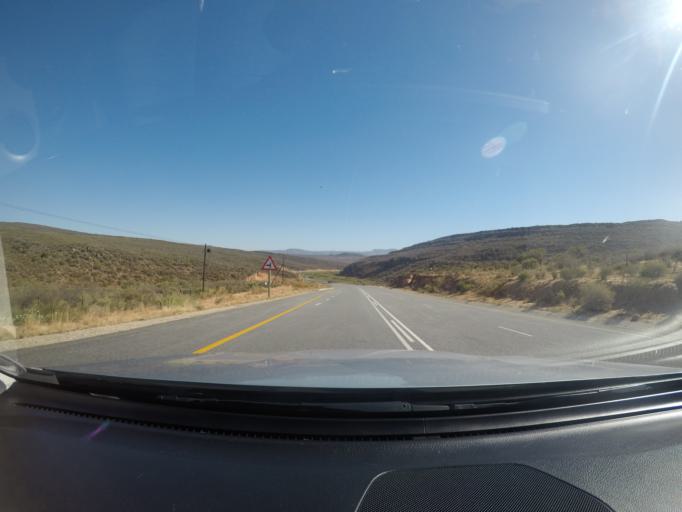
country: ZA
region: Western Cape
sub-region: West Coast District Municipality
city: Clanwilliam
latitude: -32.2282
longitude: 18.8505
